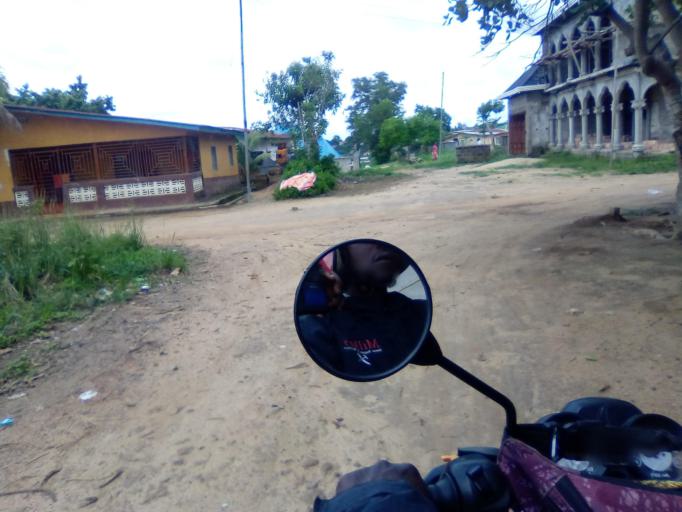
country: SL
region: Southern Province
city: Bo
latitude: 7.9417
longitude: -11.7214
